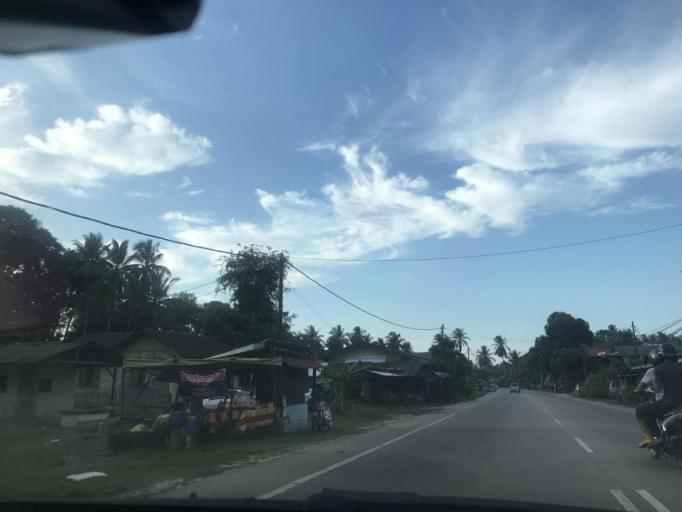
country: MY
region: Kelantan
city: Peringat
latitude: 6.1211
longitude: 102.3570
